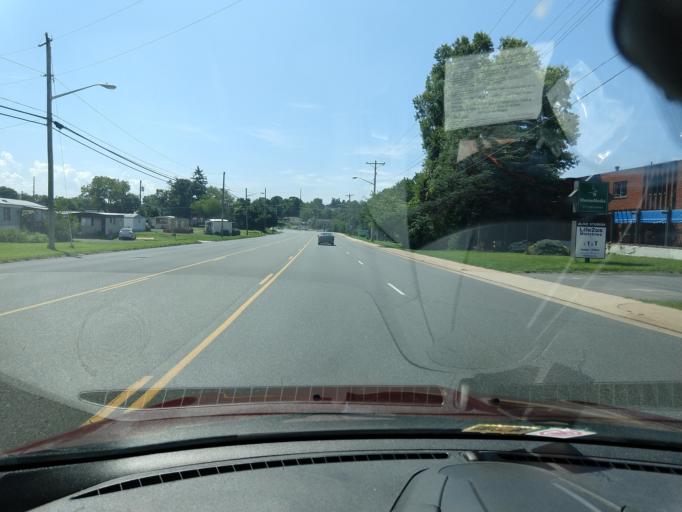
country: US
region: Virginia
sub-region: City of Harrisonburg
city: Harrisonburg
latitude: 38.4710
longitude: -78.8720
